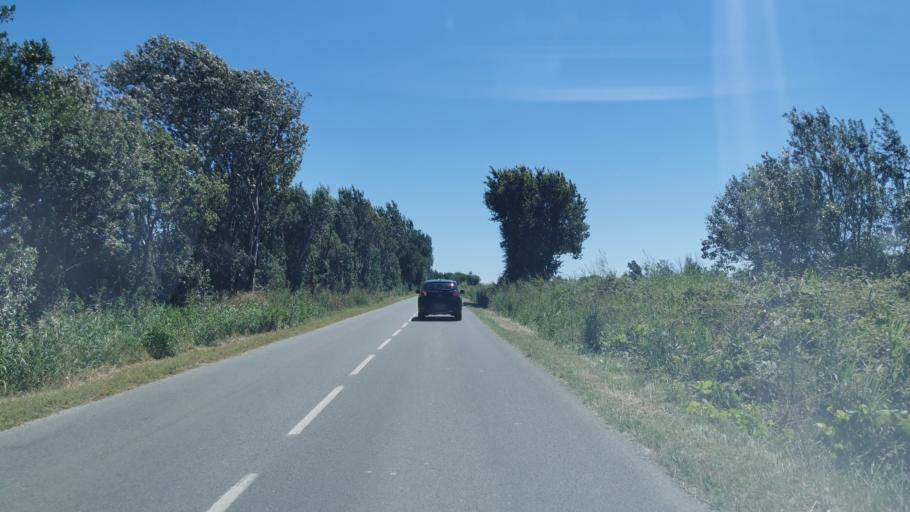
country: FR
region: Languedoc-Roussillon
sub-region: Departement de l'Aude
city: Vinassan
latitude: 43.2224
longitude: 3.0767
